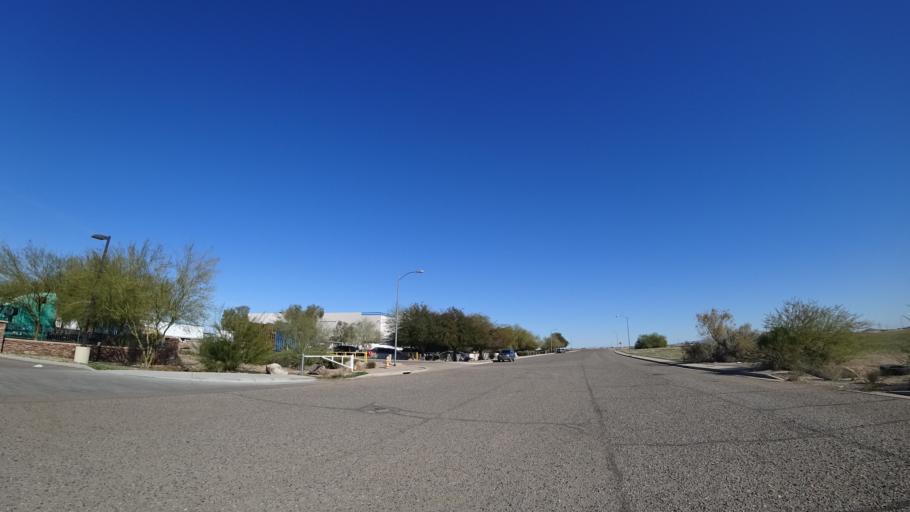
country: US
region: Arizona
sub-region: Maricopa County
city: Goodyear
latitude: 33.4138
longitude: -112.3732
